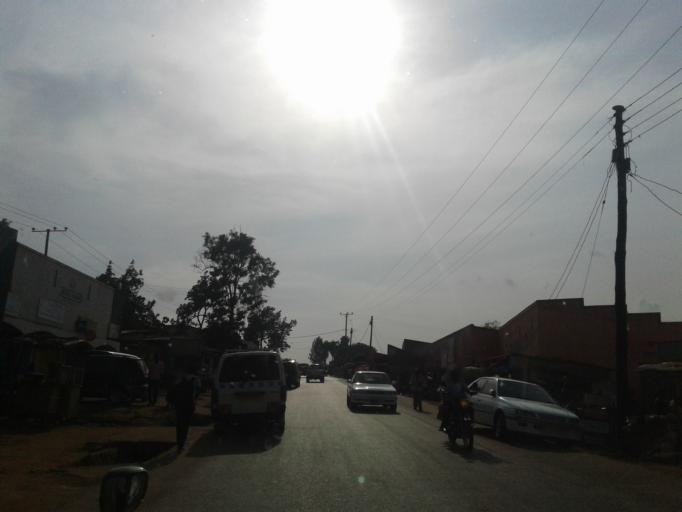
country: UG
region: Central Region
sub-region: Wakiso District
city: Kireka
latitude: 0.3343
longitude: 32.6292
